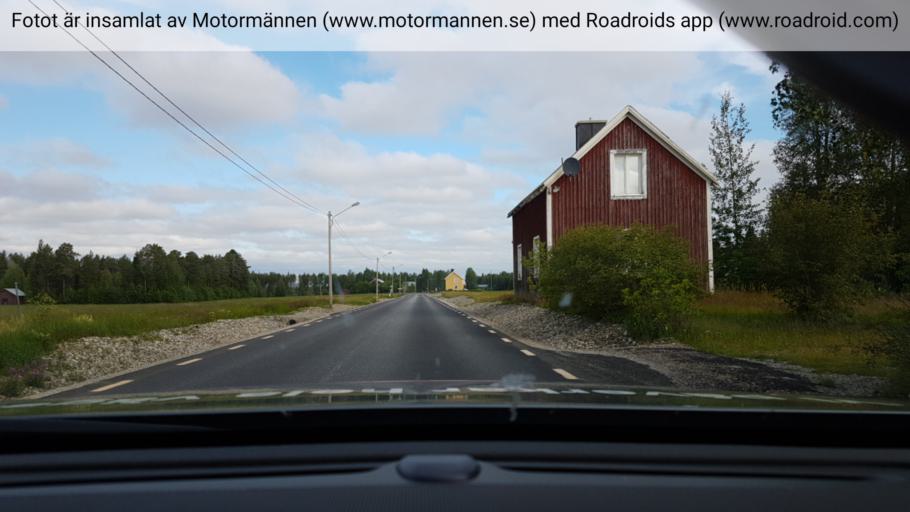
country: SE
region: Vaesterbotten
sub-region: Norsjo Kommun
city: Norsjoe
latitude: 64.5387
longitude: 19.3387
